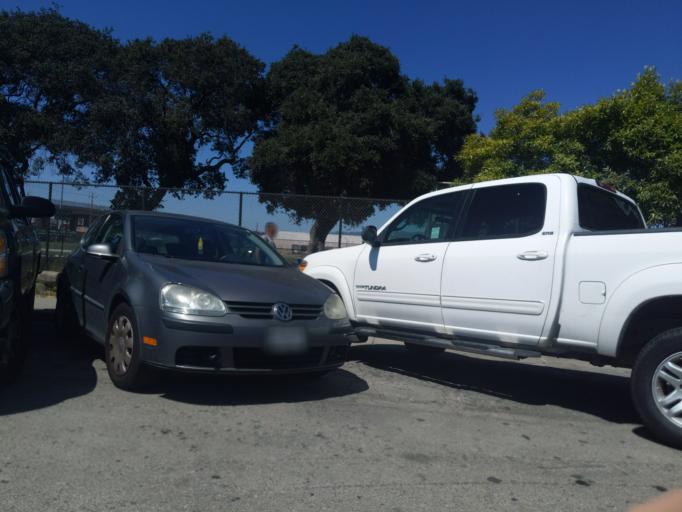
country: US
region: California
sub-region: Alameda County
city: Emeryville
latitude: 37.8157
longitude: -122.2950
